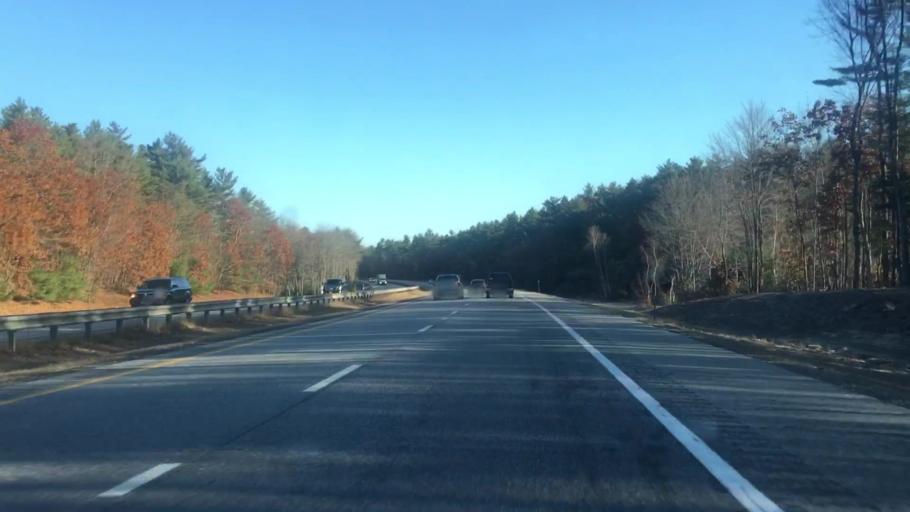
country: US
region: Maine
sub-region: Cumberland County
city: New Gloucester
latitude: 43.9776
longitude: -70.3147
